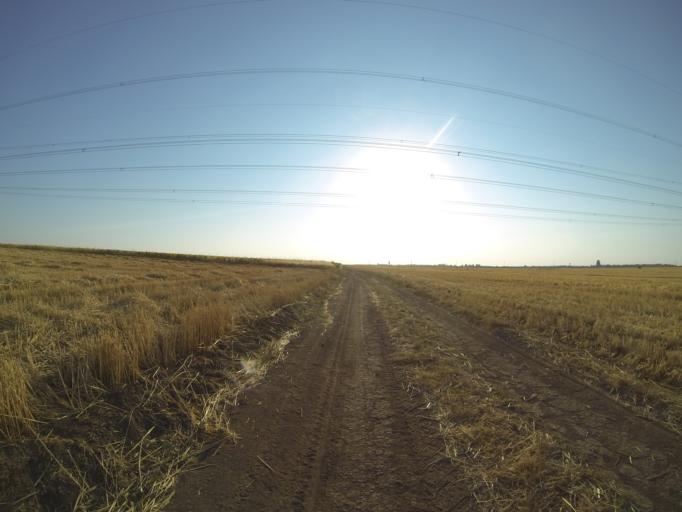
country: RO
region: Dolj
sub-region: Comuna Giurgita
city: Giurgita
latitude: 44.0291
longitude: 23.6642
